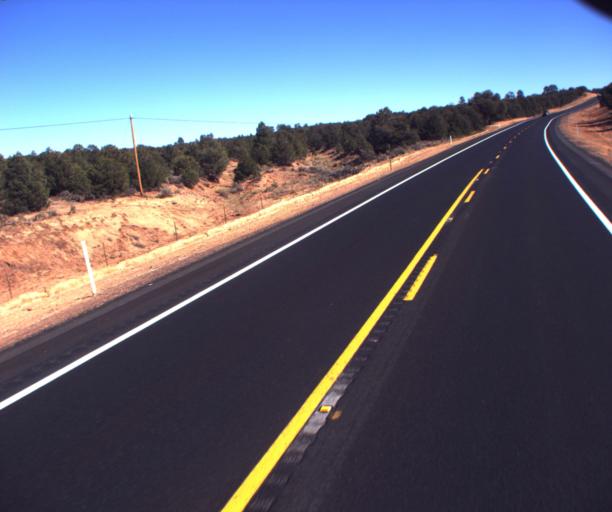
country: US
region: Arizona
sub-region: Apache County
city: Ganado
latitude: 35.7158
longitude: -109.3427
